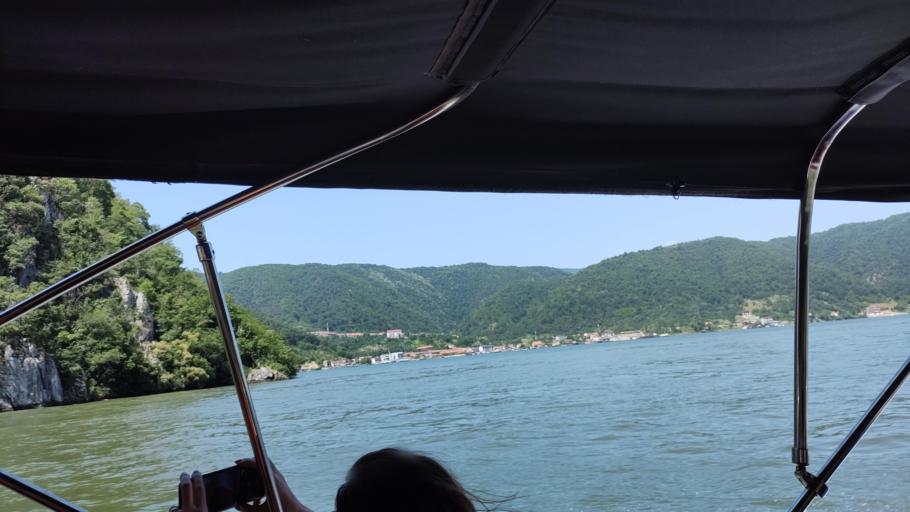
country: RO
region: Mehedinti
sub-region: Comuna Dubova
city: Dubova
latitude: 44.6174
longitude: 22.2729
